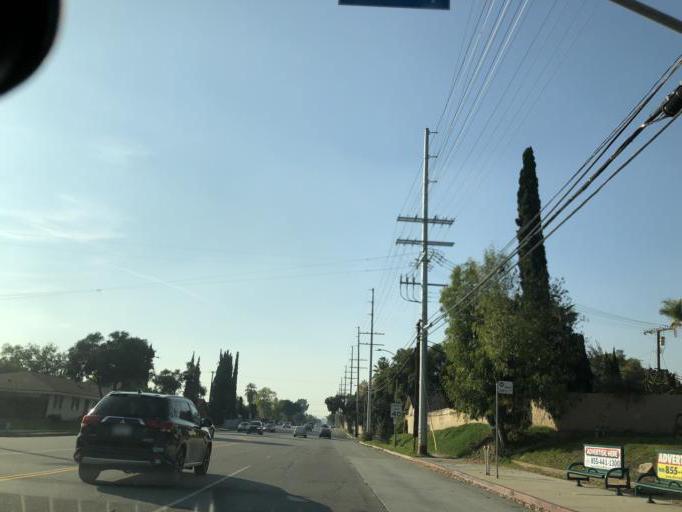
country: US
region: California
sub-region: Los Angeles County
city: San Fernando
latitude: 34.2793
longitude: -118.4847
